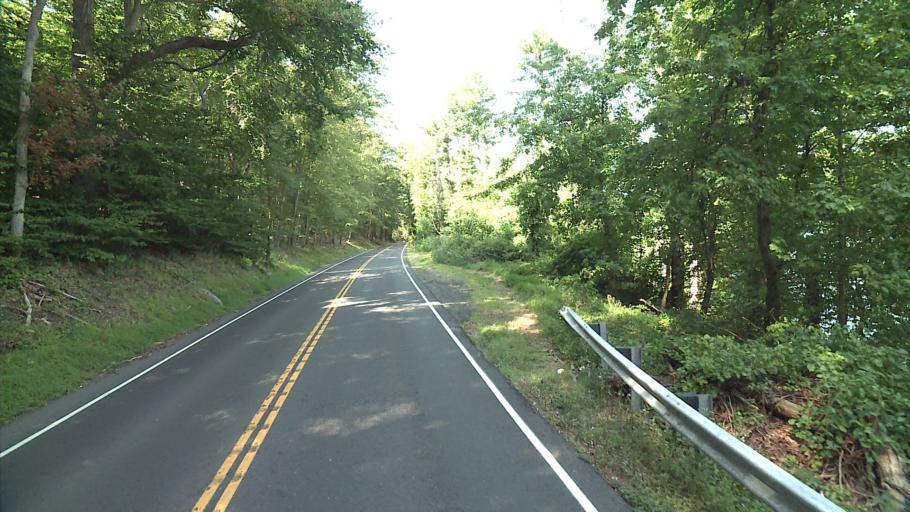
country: US
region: Connecticut
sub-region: Fairfield County
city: Southport
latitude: 41.2186
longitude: -73.2971
